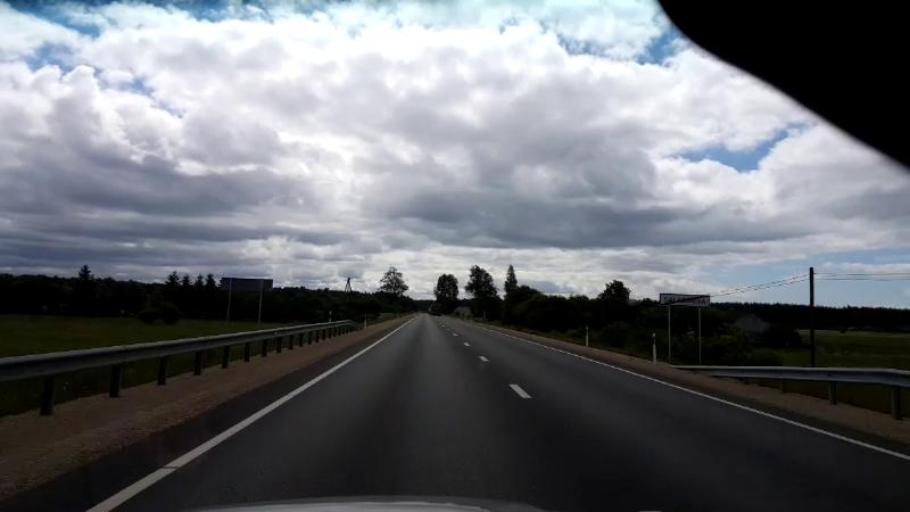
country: LV
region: Salacgrivas
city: Salacgriva
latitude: 57.7378
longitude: 24.3639
